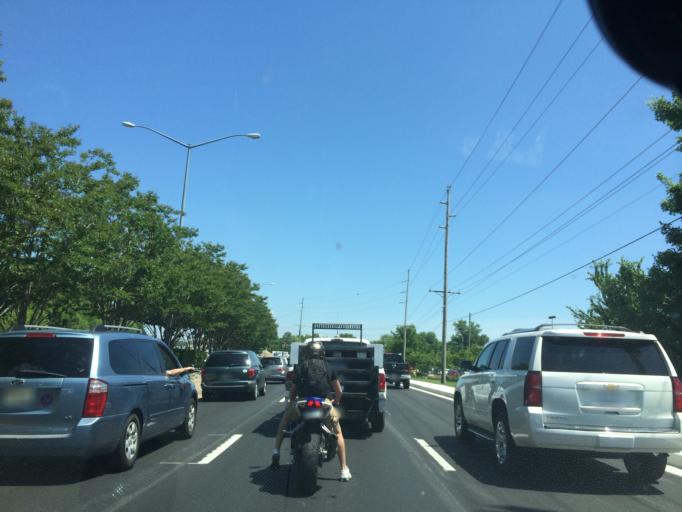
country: US
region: Maryland
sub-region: Dorchester County
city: Cambridge
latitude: 38.5550
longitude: -76.0532
